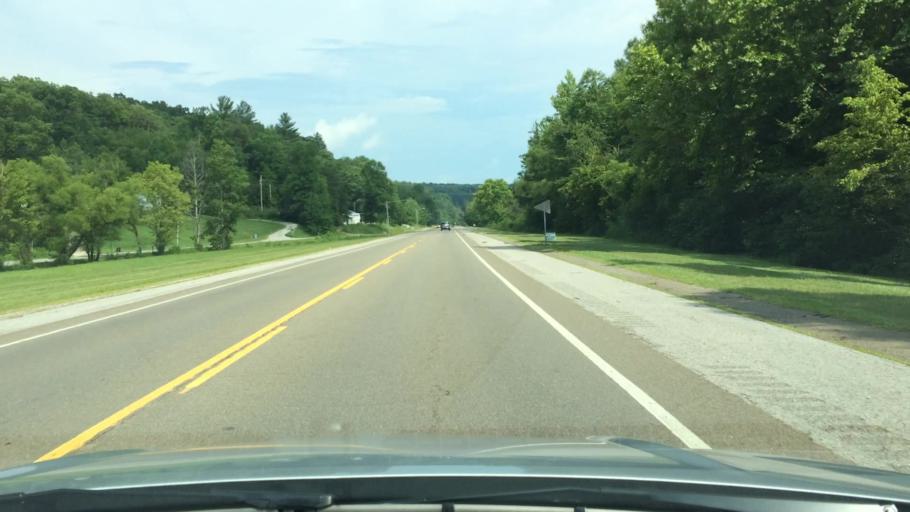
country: US
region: Tennessee
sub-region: Scott County
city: Huntsville
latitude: 36.4131
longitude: -84.4642
